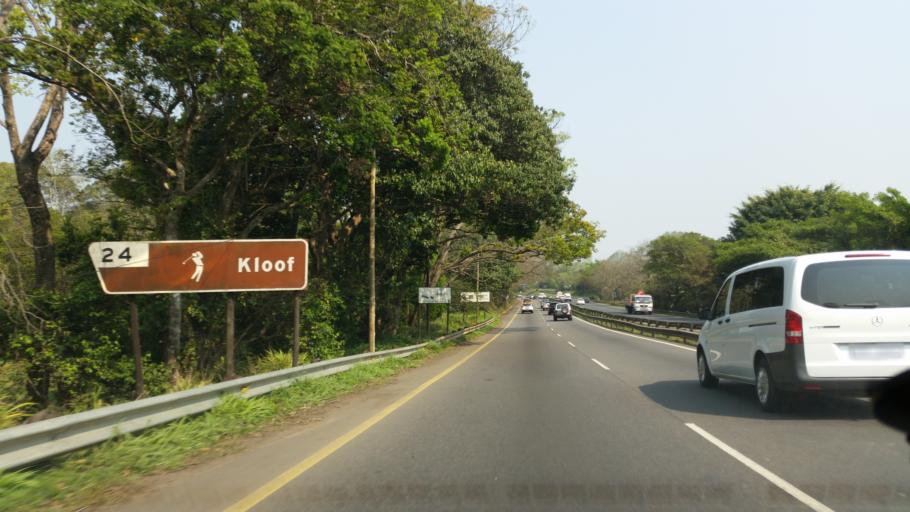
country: ZA
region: KwaZulu-Natal
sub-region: eThekwini Metropolitan Municipality
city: Berea
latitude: -29.7937
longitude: 30.8290
